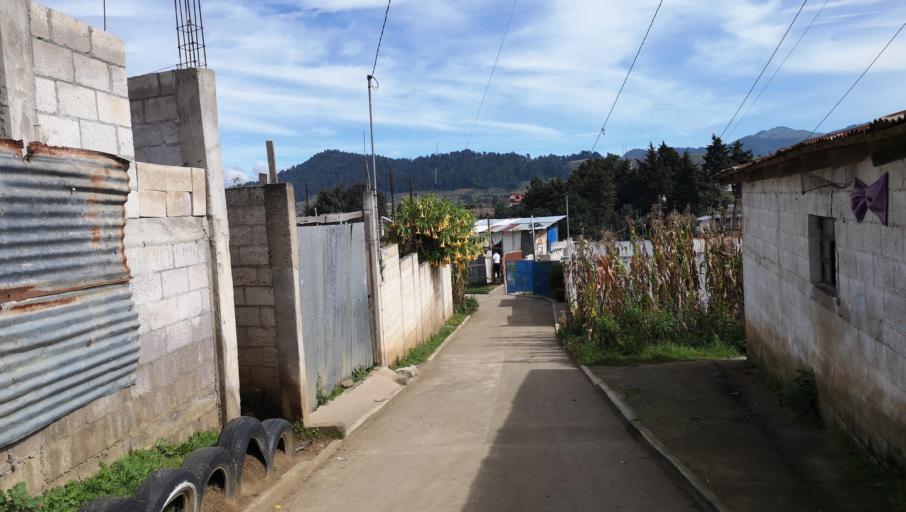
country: GT
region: Quetzaltenango
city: Cantel
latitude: 14.8186
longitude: -91.4391
